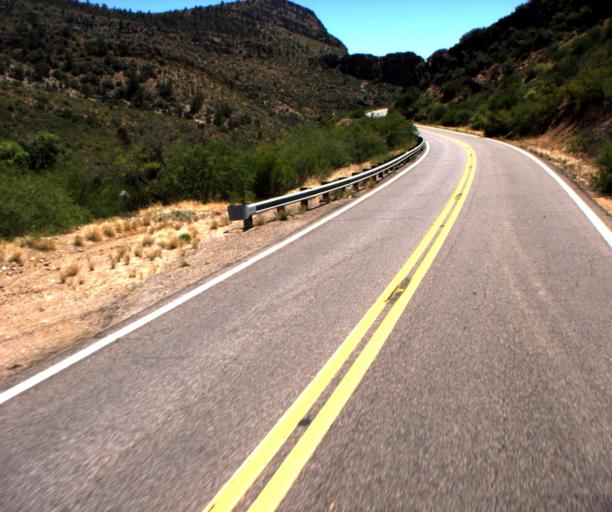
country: US
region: Arizona
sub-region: Pinal County
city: Kearny
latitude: 33.1951
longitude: -110.8053
